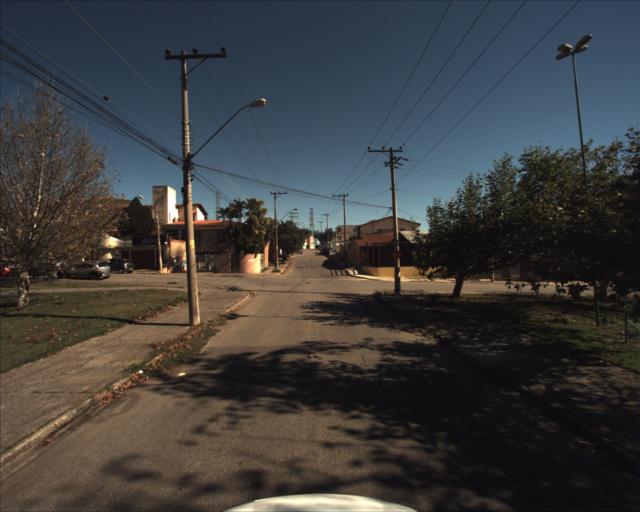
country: BR
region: Sao Paulo
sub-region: Sorocaba
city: Sorocaba
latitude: -23.5120
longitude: -47.4955
